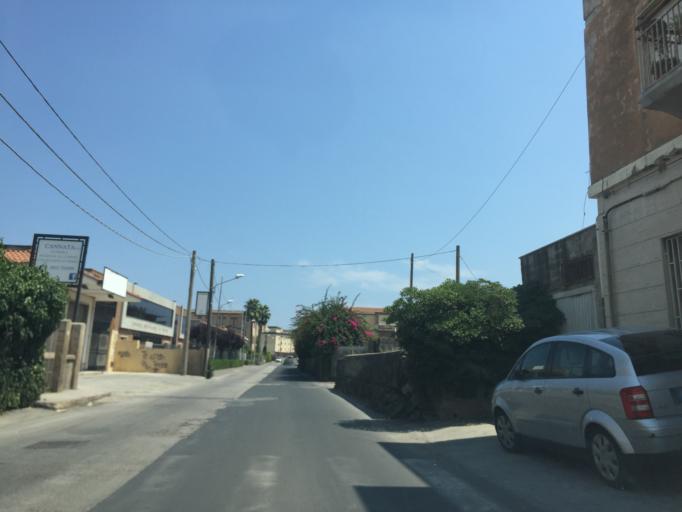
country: IT
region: Sicily
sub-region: Provincia di Siracusa
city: Siracusa
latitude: 37.0694
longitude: 15.2760
